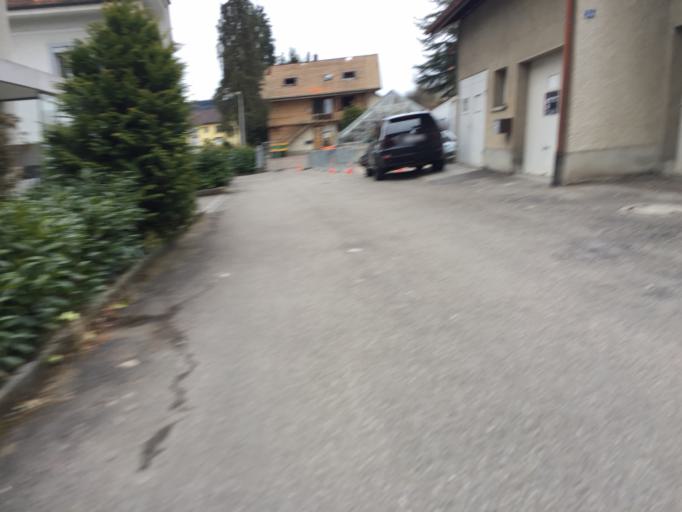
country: CH
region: Bern
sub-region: Bern-Mittelland District
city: Koniz
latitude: 46.9205
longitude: 7.4091
